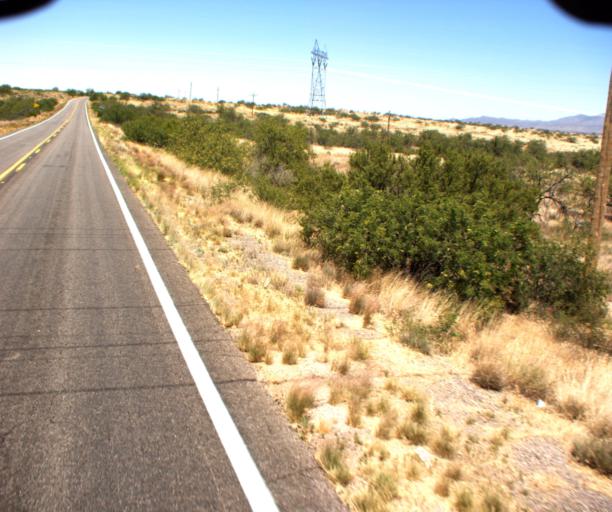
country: US
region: Arizona
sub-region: Pima County
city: Catalina
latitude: 32.6027
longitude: -110.9820
